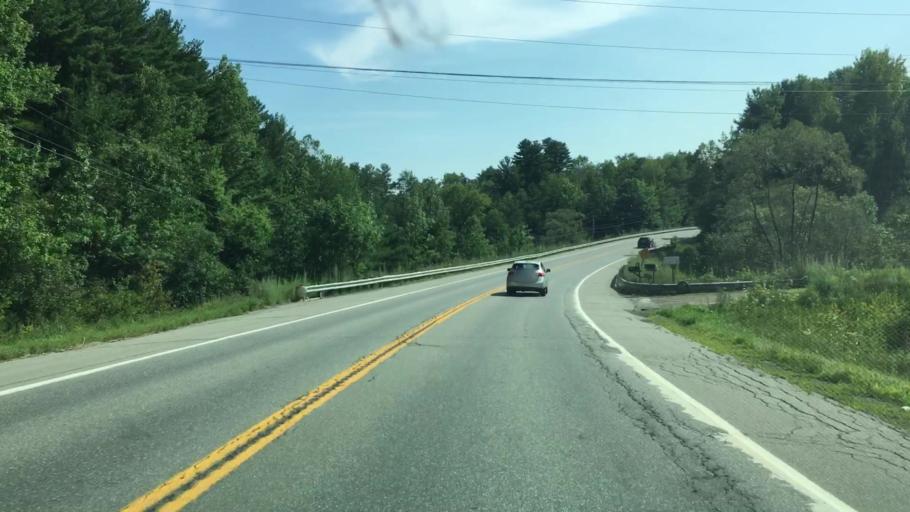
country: US
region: Maine
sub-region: Penobscot County
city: Orrington
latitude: 44.7002
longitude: -68.8442
